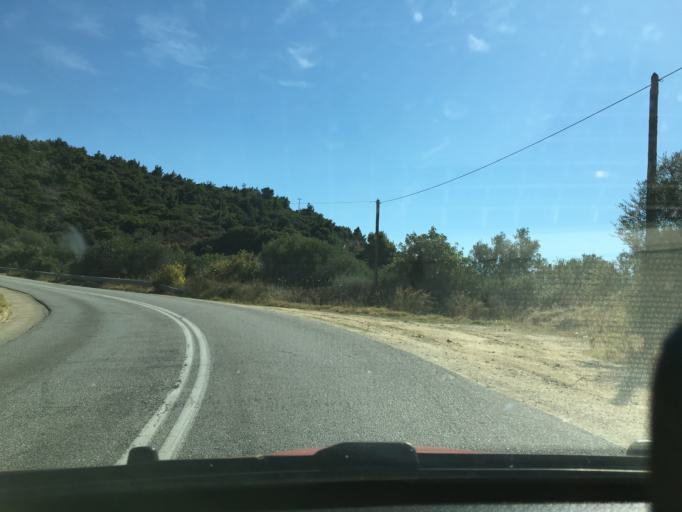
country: GR
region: Central Macedonia
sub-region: Nomos Chalkidikis
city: Ouranoupolis
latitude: 40.3370
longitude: 23.9714
